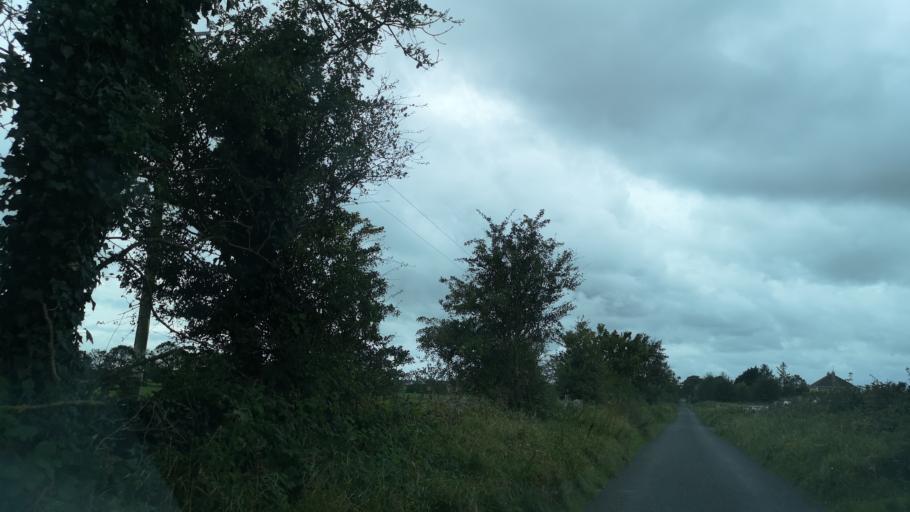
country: IE
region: Connaught
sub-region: County Galway
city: Athenry
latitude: 53.3241
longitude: -8.7496
